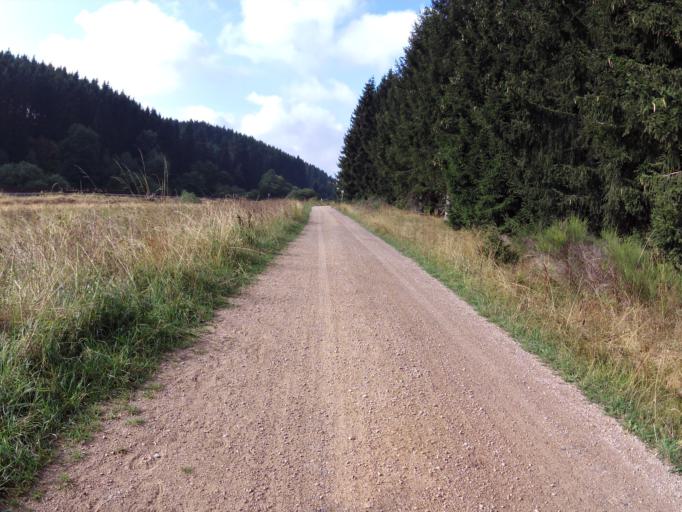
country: DE
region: North Rhine-Westphalia
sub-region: Regierungsbezirk Koln
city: Nettersheim
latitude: 50.4540
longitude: 6.6081
